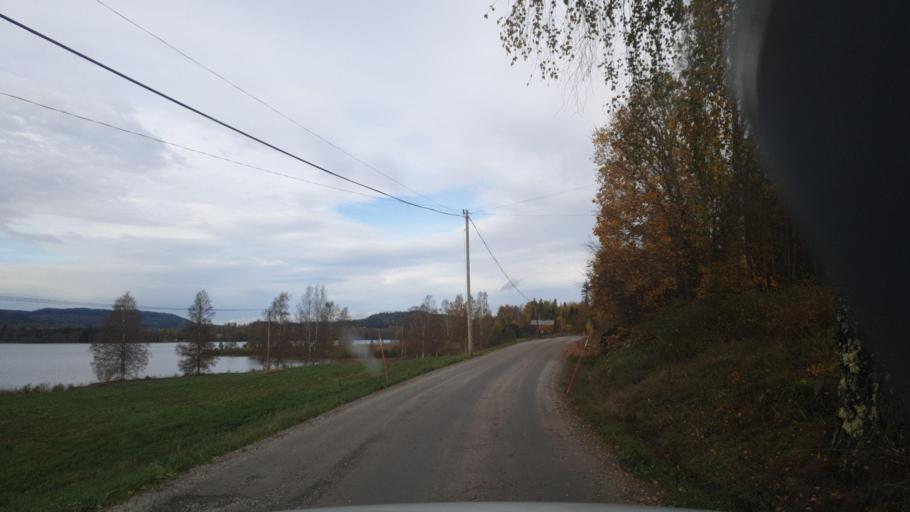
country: SE
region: Vaermland
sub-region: Arvika Kommun
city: Arvika
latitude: 59.7303
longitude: 12.8332
